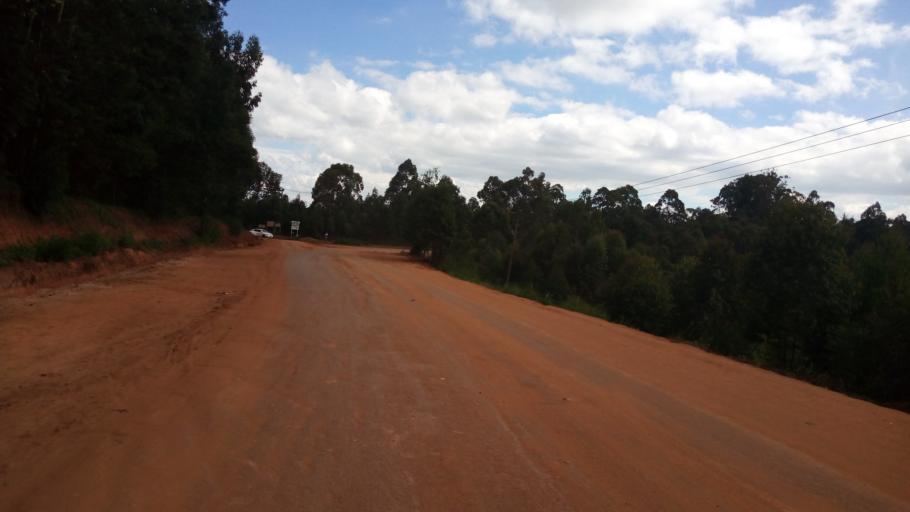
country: KE
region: Makueni
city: Wote
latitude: -1.6565
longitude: 37.4537
